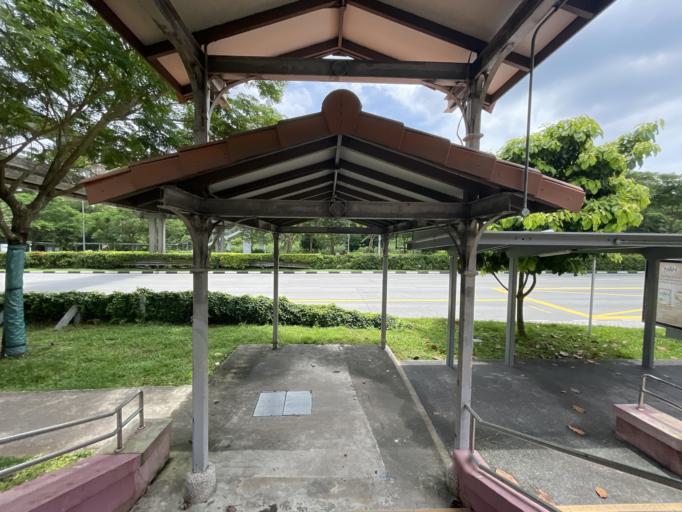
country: SG
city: Singapore
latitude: 1.3149
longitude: 103.7717
